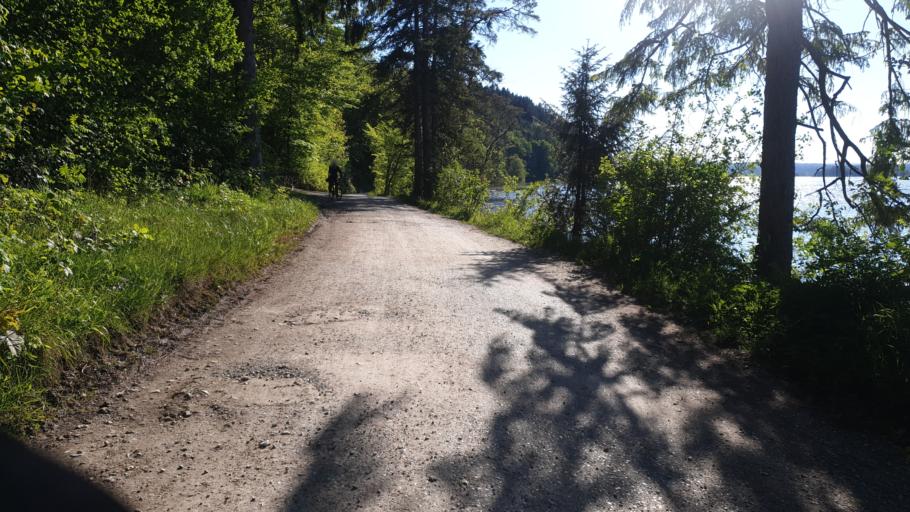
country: DE
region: Bavaria
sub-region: Upper Bavaria
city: Seehausen am Staffelsee
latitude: 47.6787
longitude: 11.1775
